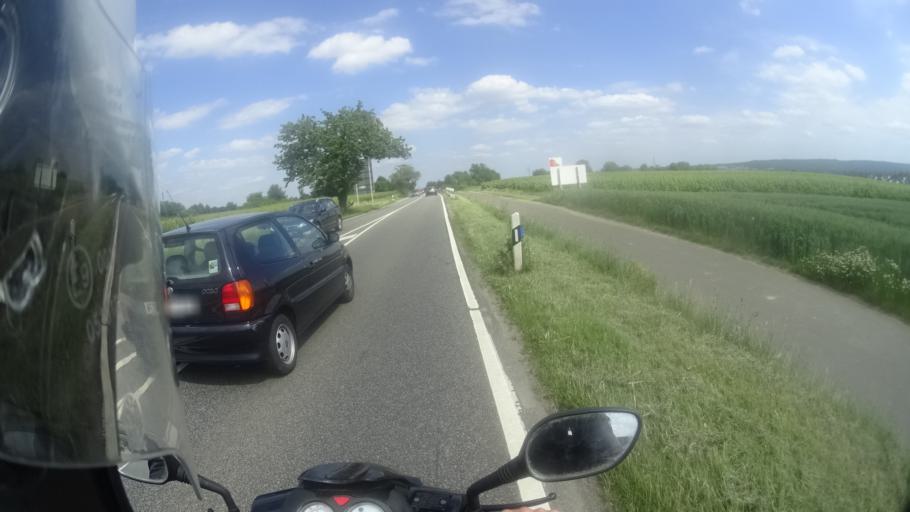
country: DE
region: Hesse
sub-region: Regierungsbezirk Darmstadt
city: Walluf
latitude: 50.0453
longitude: 8.1458
